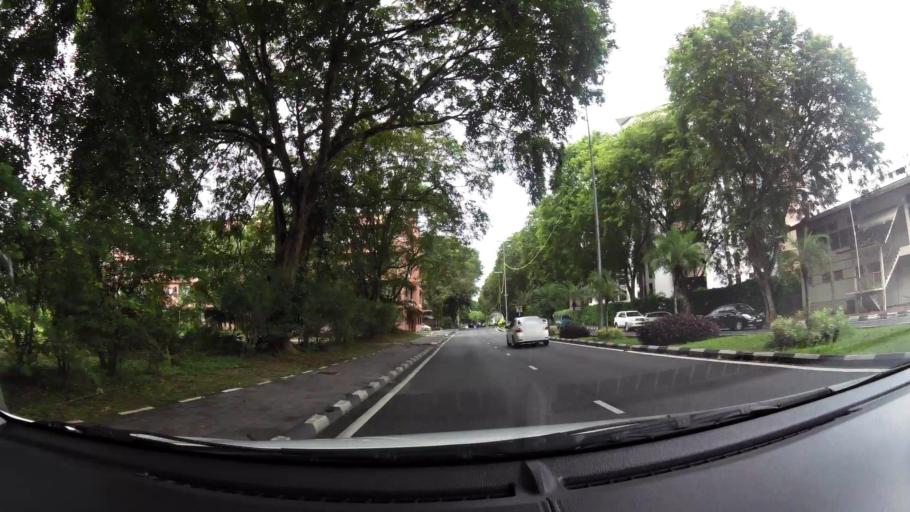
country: BN
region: Brunei and Muara
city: Bandar Seri Begawan
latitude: 4.8971
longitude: 114.9406
